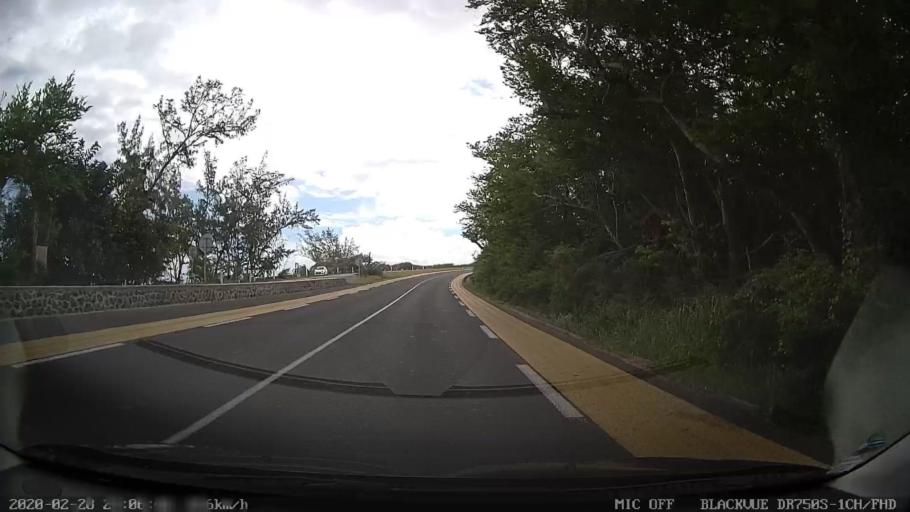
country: RE
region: Reunion
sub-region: Reunion
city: Saint-Leu
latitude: -21.1508
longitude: 55.2770
